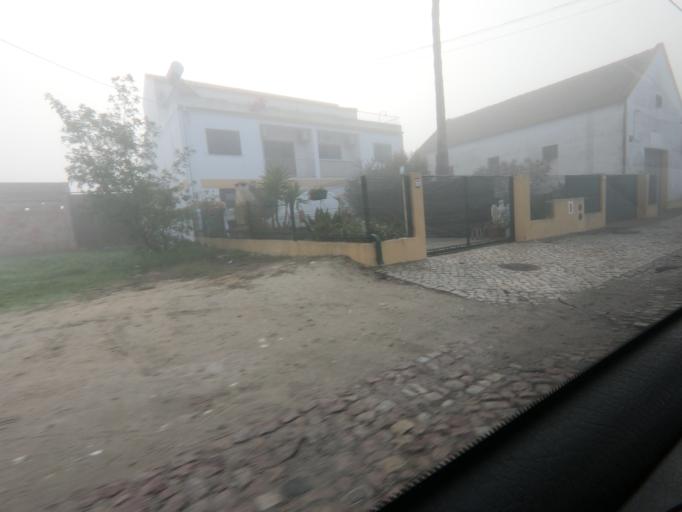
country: PT
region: Setubal
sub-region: Palmela
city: Palmela
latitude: 38.5732
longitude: -8.8332
